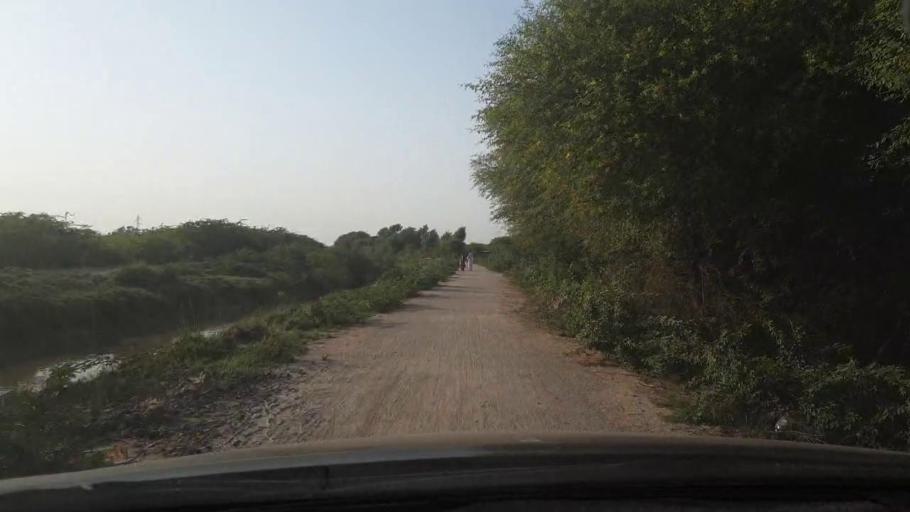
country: PK
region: Sindh
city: Naukot
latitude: 24.7644
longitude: 69.2273
